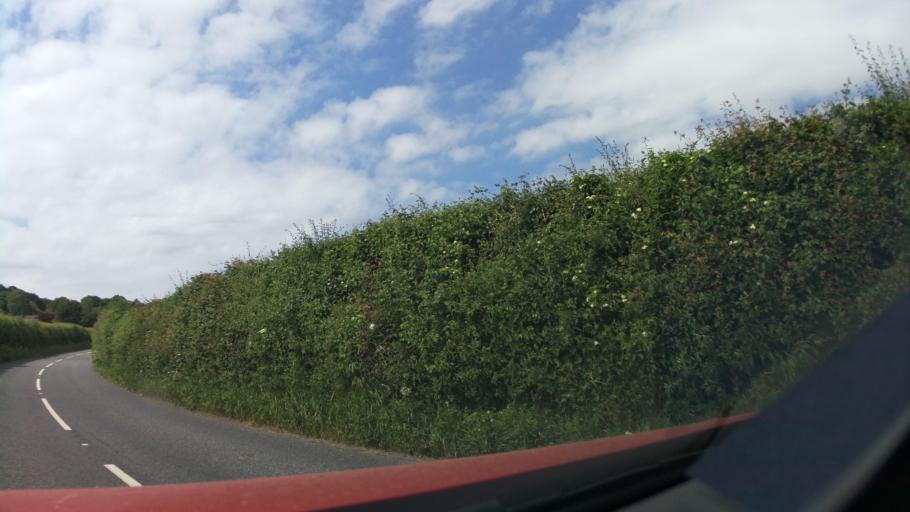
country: GB
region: England
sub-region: Somerset
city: Wincanton
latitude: 51.0354
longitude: -2.4411
